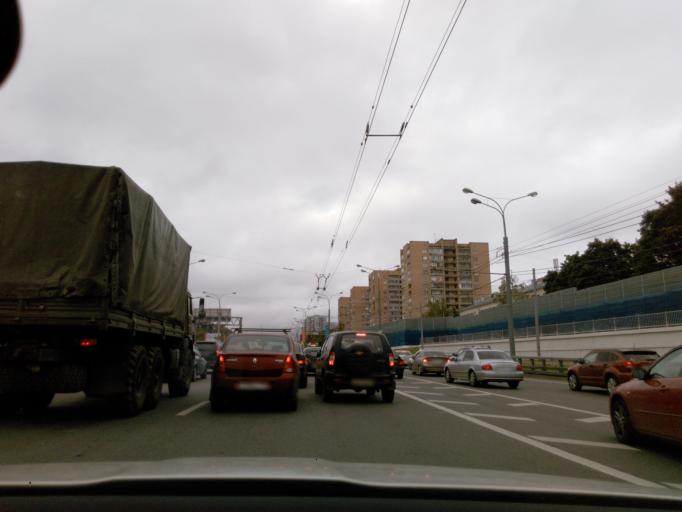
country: RU
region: Moscow
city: Pokrovskoye-Streshnevo
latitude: 55.8180
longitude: 37.4569
